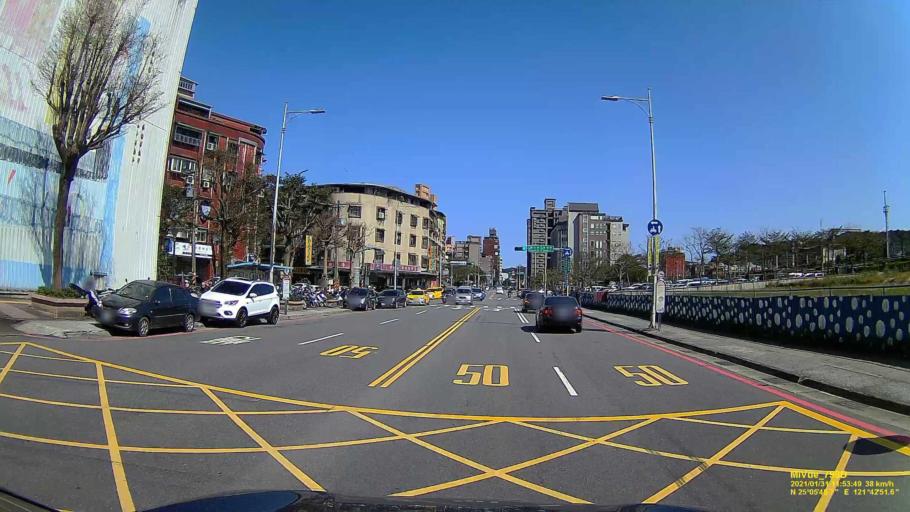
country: TW
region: Taiwan
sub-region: Keelung
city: Keelung
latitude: 25.0962
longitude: 121.7145
